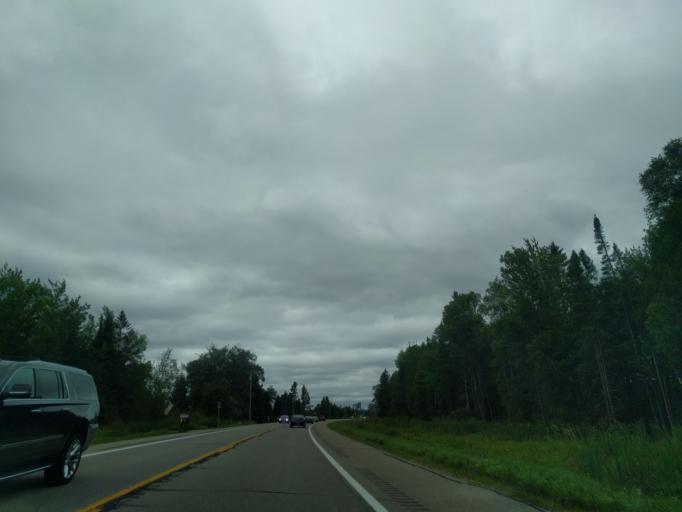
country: US
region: Michigan
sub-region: Delta County
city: Escanaba
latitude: 45.6438
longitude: -87.1899
